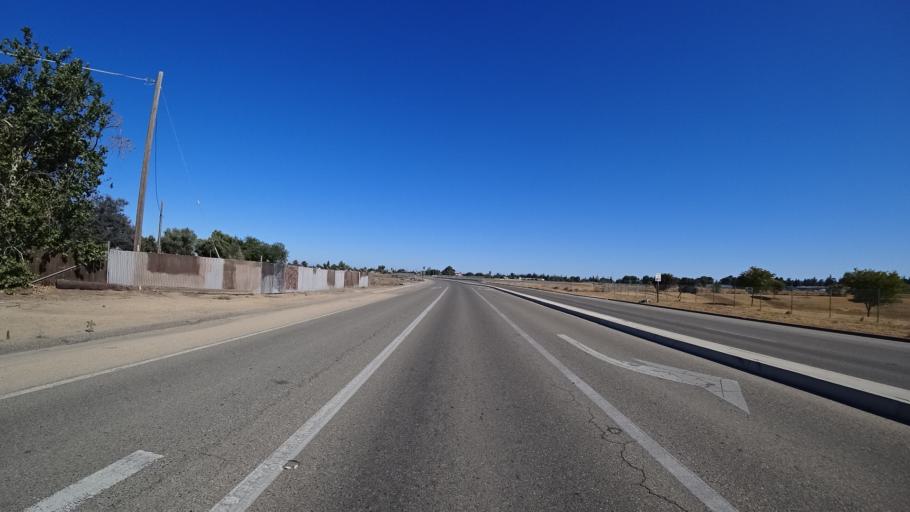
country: US
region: California
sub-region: Fresno County
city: West Park
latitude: 36.7365
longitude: -119.8304
